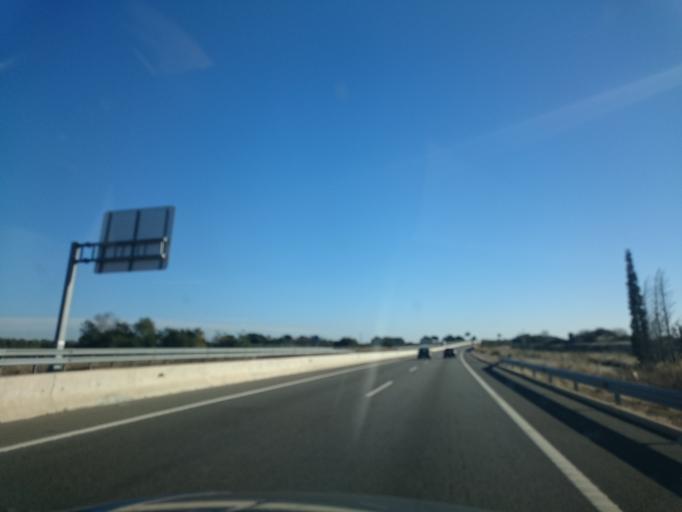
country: ES
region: Catalonia
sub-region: Provincia de Tarragona
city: Cambrils
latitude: 41.0855
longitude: 1.0483
